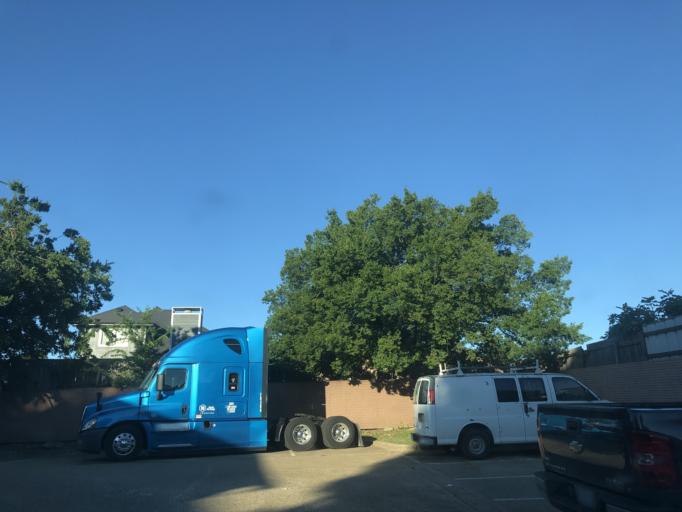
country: US
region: Texas
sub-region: Dallas County
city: Garland
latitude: 32.8377
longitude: -96.6355
